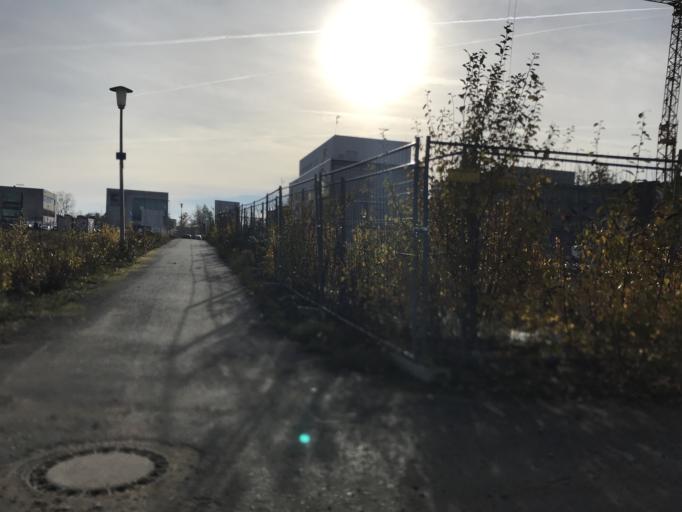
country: DE
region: North Rhine-Westphalia
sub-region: Regierungsbezirk Arnsberg
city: Hamm
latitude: 51.6846
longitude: 7.8387
